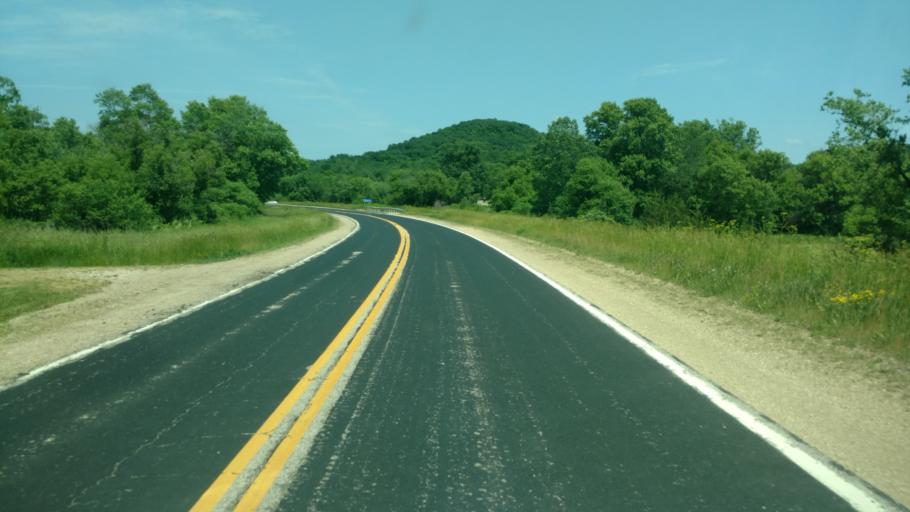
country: US
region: Wisconsin
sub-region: Monroe County
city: Cashton
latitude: 43.5564
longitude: -90.6498
